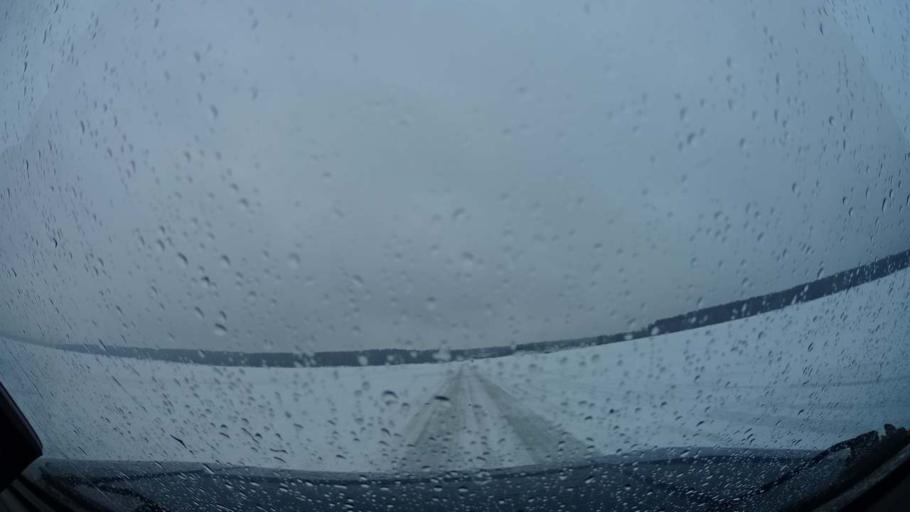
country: RU
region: Tverskaya
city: Konakovo
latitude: 56.7023
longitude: 36.7254
